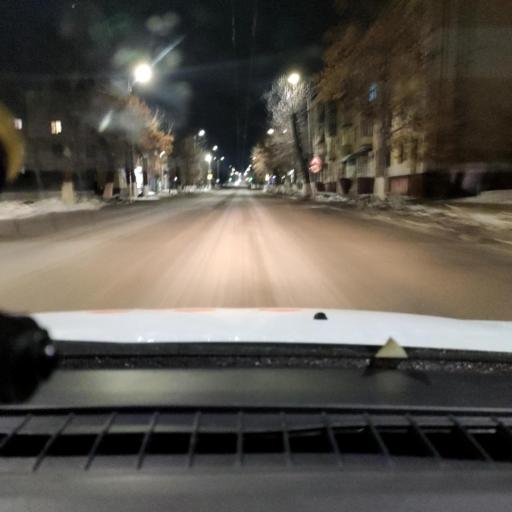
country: RU
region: Samara
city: Novokuybyshevsk
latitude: 53.0941
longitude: 49.9495
